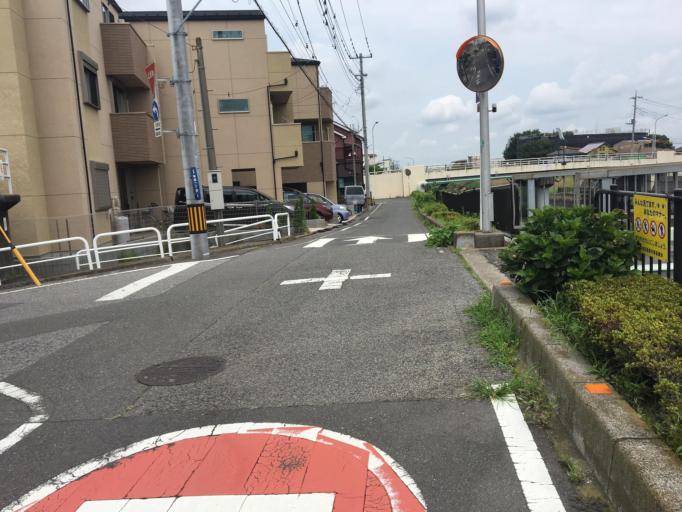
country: JP
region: Saitama
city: Shimotoda
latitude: 35.8163
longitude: 139.6570
